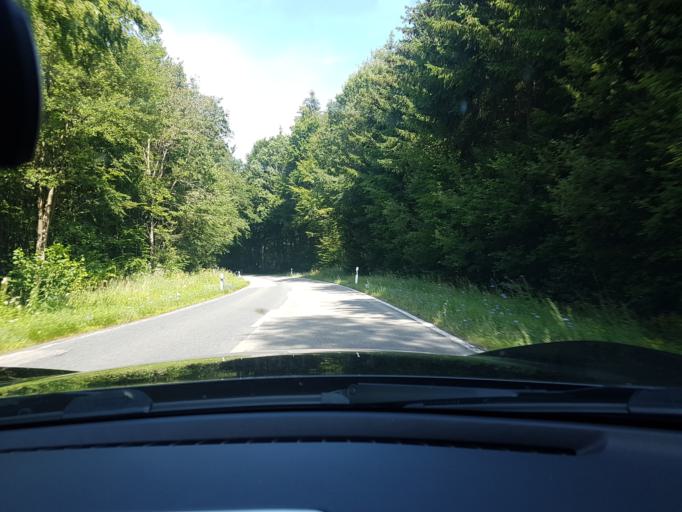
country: DE
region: Baden-Wuerttemberg
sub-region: Karlsruhe Region
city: Limbach
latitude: 49.4562
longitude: 9.2656
